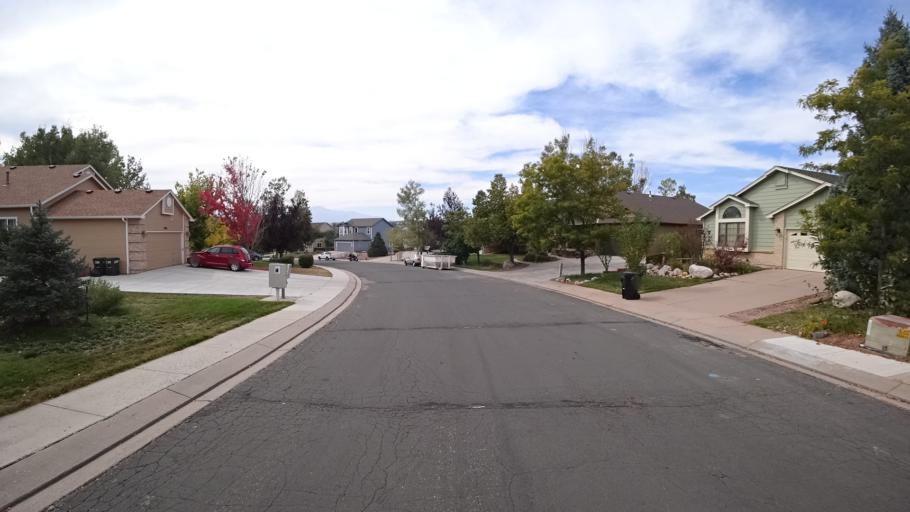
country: US
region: Colorado
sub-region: El Paso County
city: Cimarron Hills
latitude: 38.9029
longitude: -104.7028
